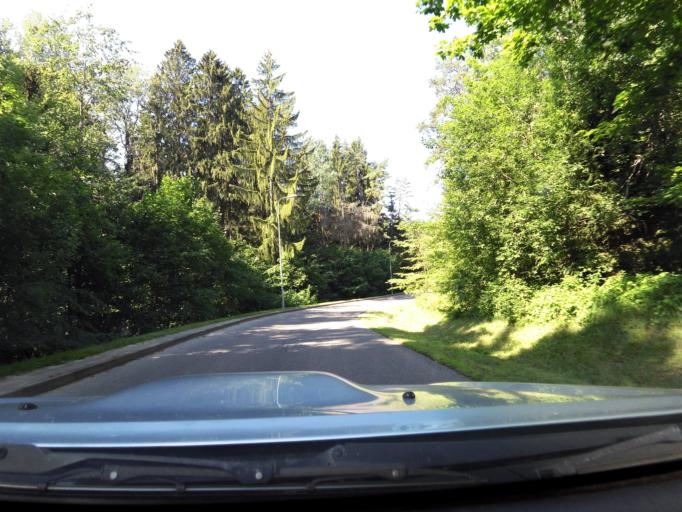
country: LT
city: Birstonas
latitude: 54.6053
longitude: 24.0004
